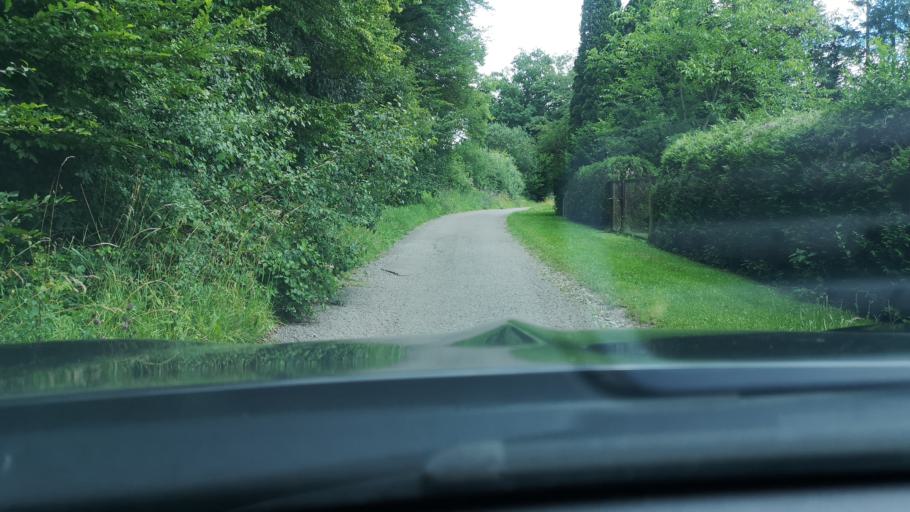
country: DE
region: Baden-Wuerttemberg
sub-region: Regierungsbezirk Stuttgart
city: Leinfelden-Echterdingen
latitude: 48.6622
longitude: 9.1606
